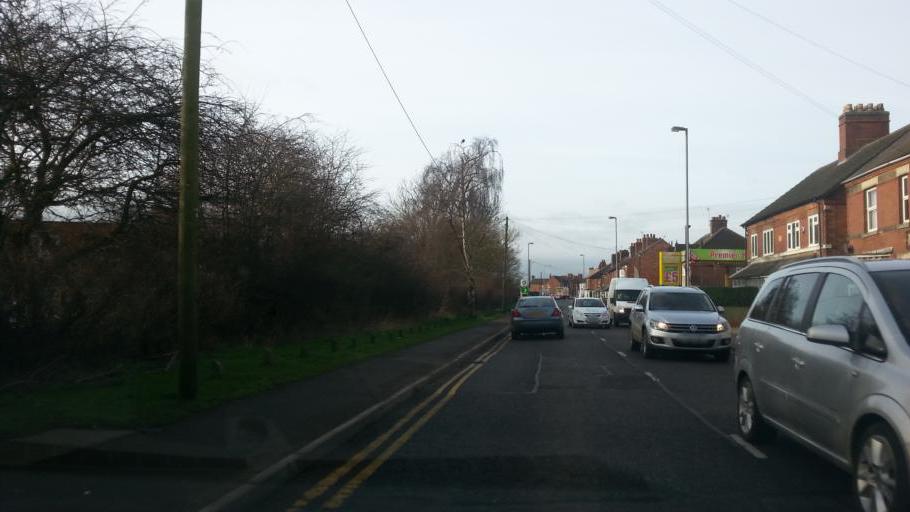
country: GB
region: England
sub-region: Leicestershire
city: Melton Mowbray
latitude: 52.7689
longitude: -0.8728
